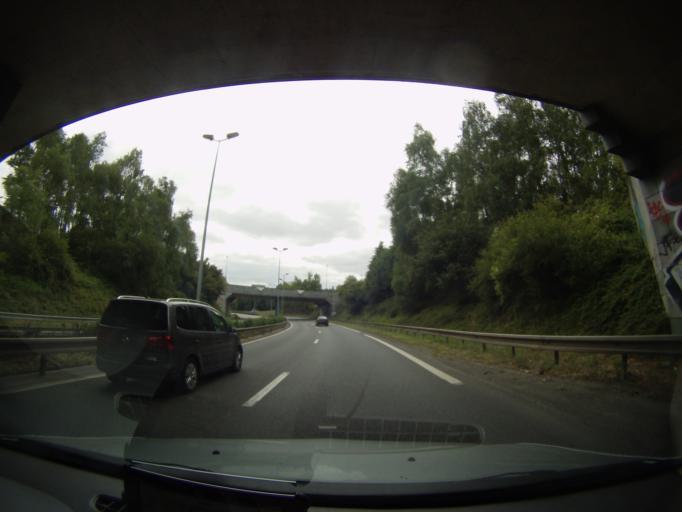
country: FR
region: Pays de la Loire
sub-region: Departement de la Loire-Atlantique
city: La Chapelle-sur-Erdre
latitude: 47.2603
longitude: -1.5568
